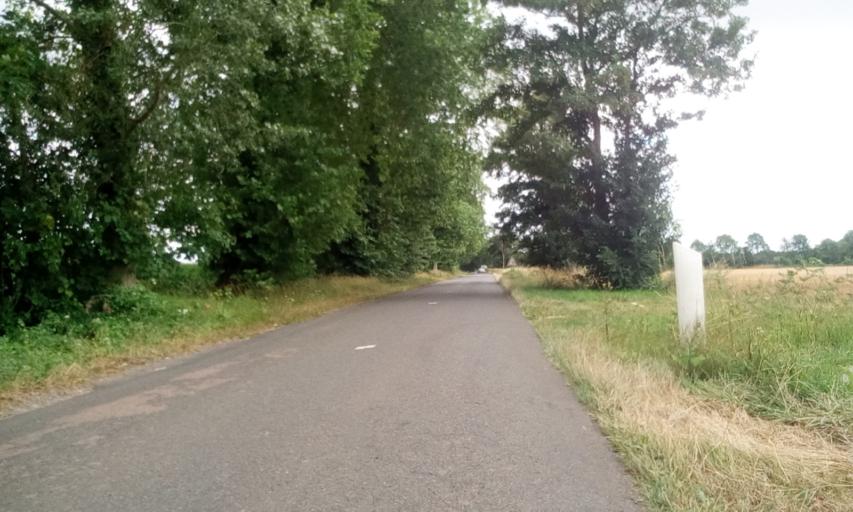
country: FR
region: Lower Normandy
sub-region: Departement du Calvados
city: Bellengreville
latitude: 49.1406
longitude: -0.2061
